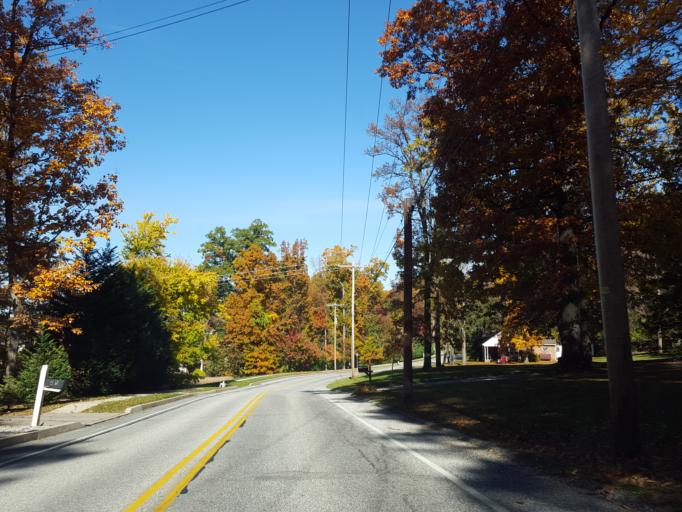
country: US
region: Pennsylvania
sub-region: York County
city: Spry
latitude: 39.9232
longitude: -76.6608
